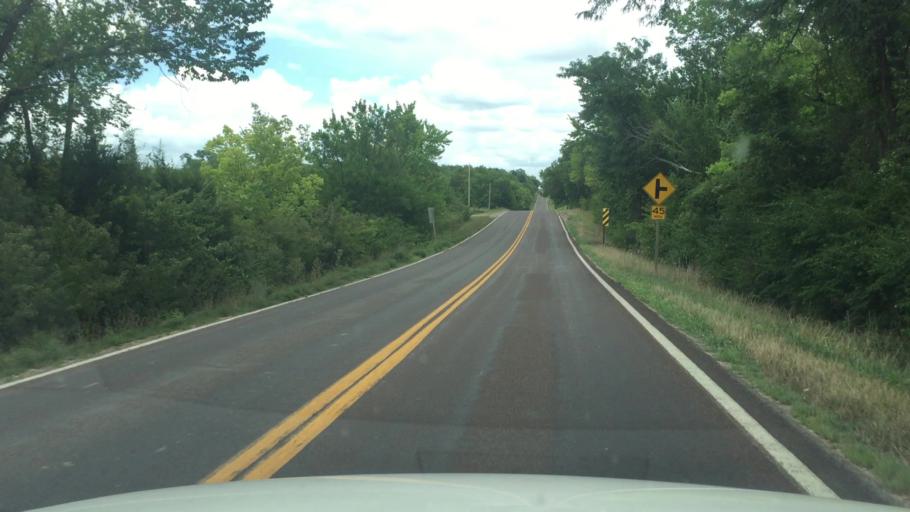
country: US
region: Kansas
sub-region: Shawnee County
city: Topeka
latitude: 39.0294
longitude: -95.5227
